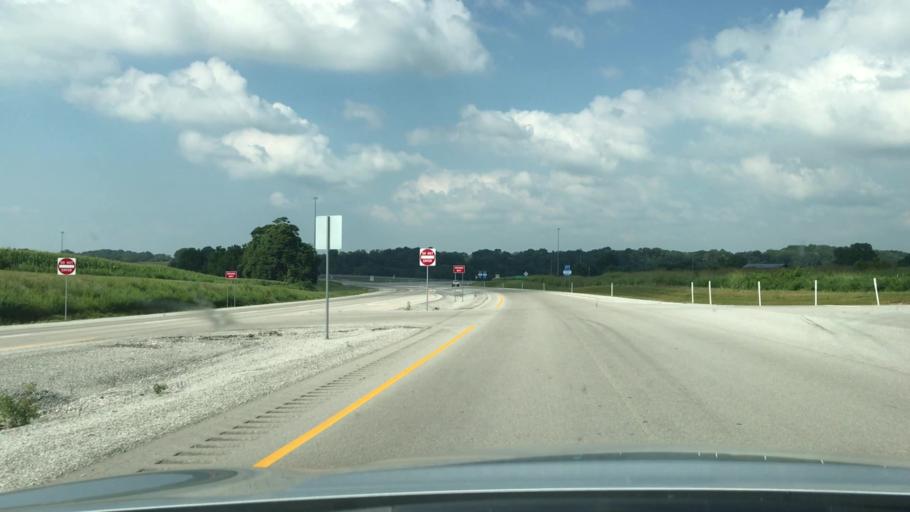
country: US
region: Kentucky
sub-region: Barren County
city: Glasgow
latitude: 36.9969
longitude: -85.9760
